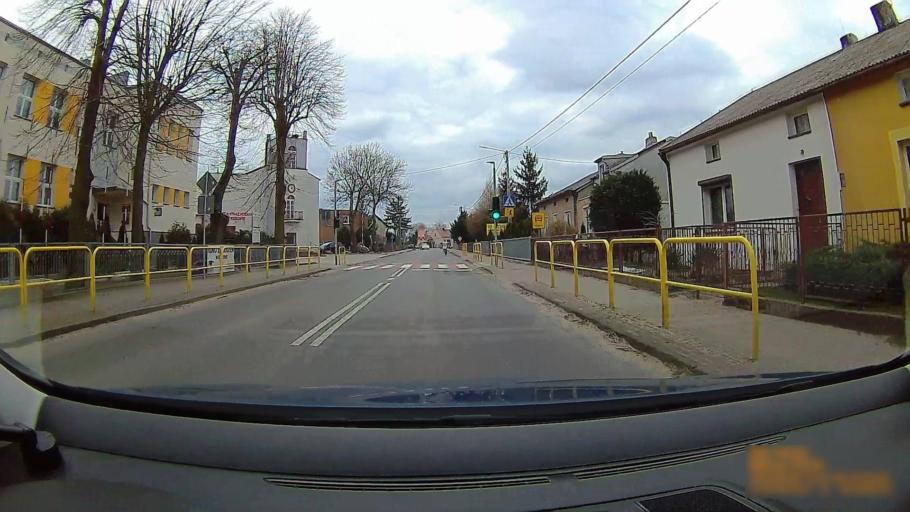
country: PL
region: Greater Poland Voivodeship
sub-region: Powiat koninski
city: Rzgow Pierwszy
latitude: 52.1544
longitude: 18.0523
